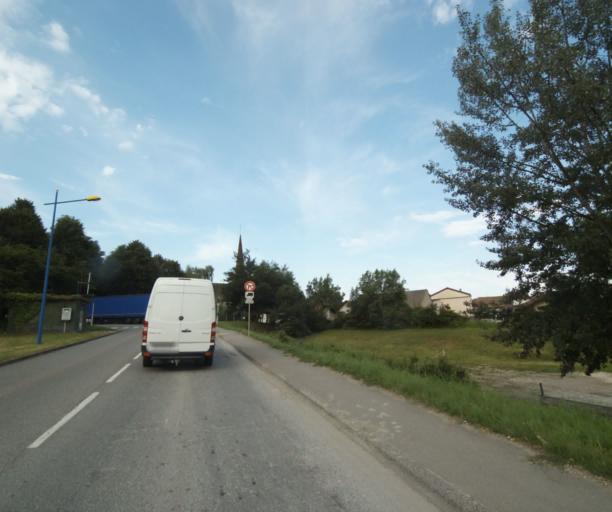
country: FR
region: Rhone-Alpes
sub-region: Departement de la Haute-Savoie
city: Marin
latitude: 46.3834
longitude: 6.5065
